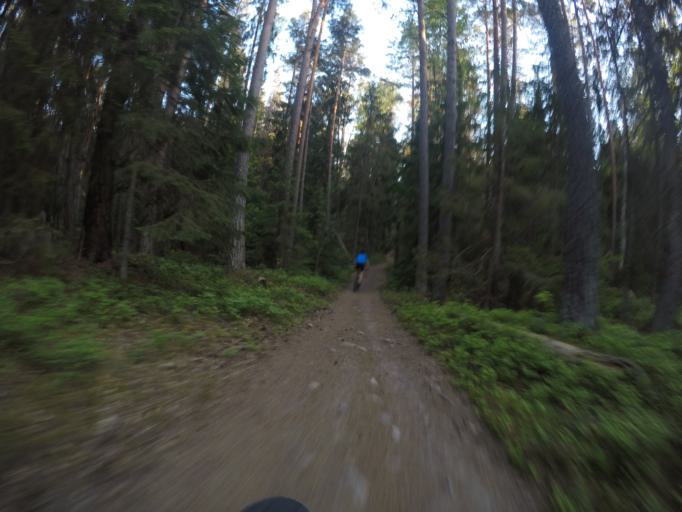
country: SE
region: Soedermanland
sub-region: Eskilstuna Kommun
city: Skogstorp
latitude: 59.3325
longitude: 16.5146
